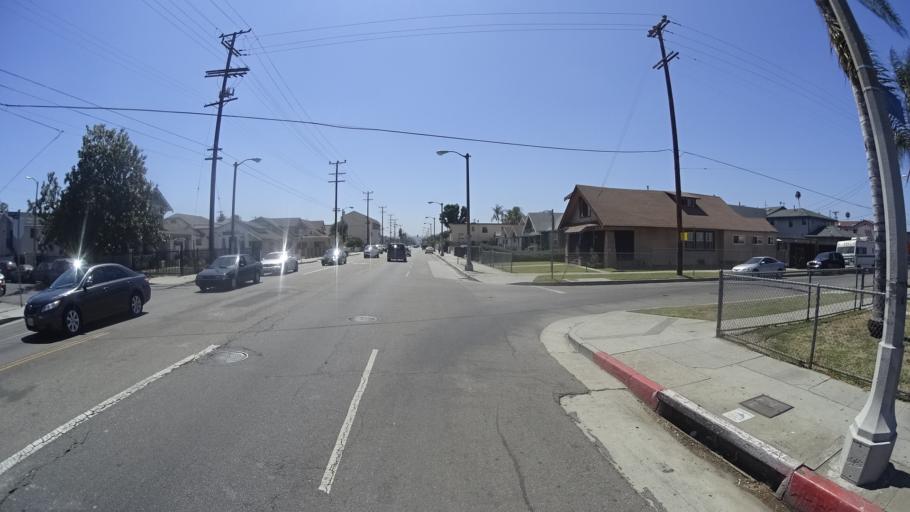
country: US
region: California
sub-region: Los Angeles County
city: View Park-Windsor Hills
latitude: 34.0035
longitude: -118.2931
